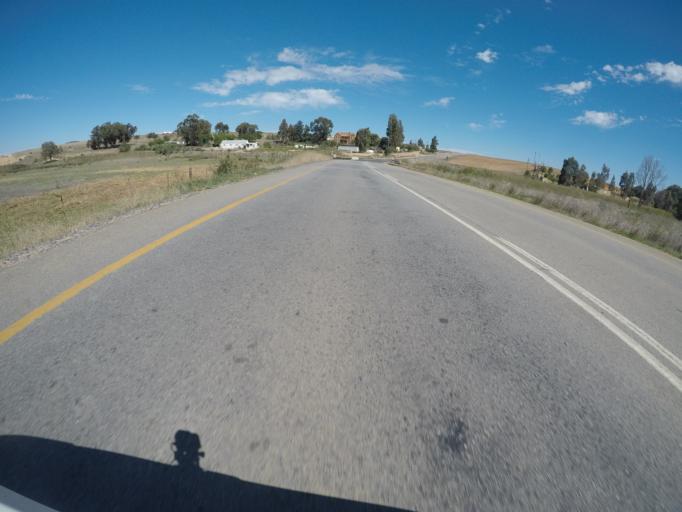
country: ZA
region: Western Cape
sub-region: West Coast District Municipality
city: Malmesbury
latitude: -33.4779
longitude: 18.7146
